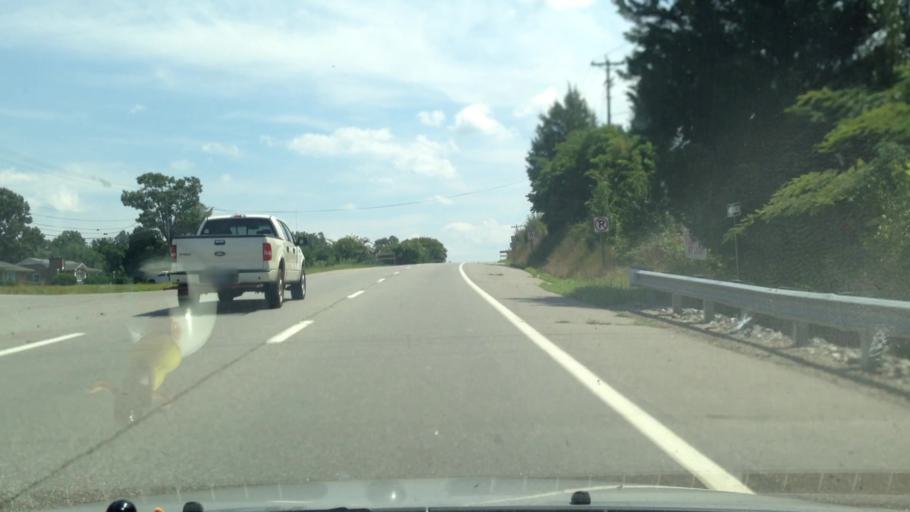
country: US
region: Virginia
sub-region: Henry County
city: Chatmoss
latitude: 36.6353
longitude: -79.8590
